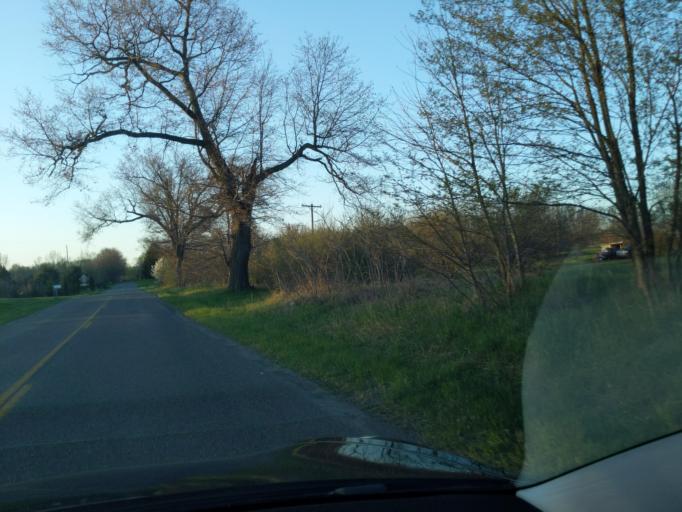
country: US
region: Michigan
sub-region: Ingham County
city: Stockbridge
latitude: 42.4905
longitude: -84.2945
